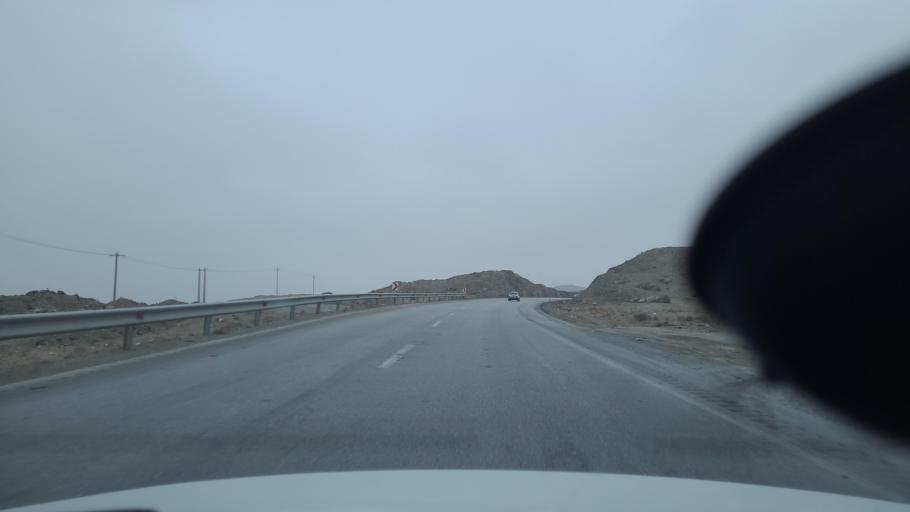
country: IR
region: Razavi Khorasan
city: Fariman
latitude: 35.9950
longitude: 59.7562
